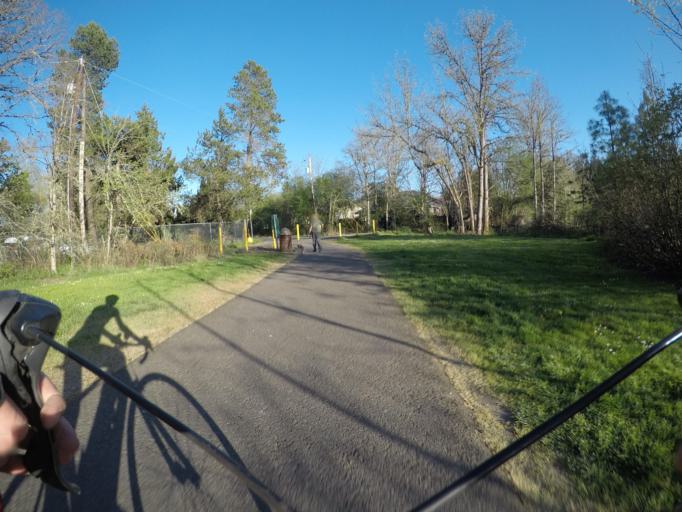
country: US
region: Oregon
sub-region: Washington County
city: Oak Hills
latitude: 45.5216
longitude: -122.8340
